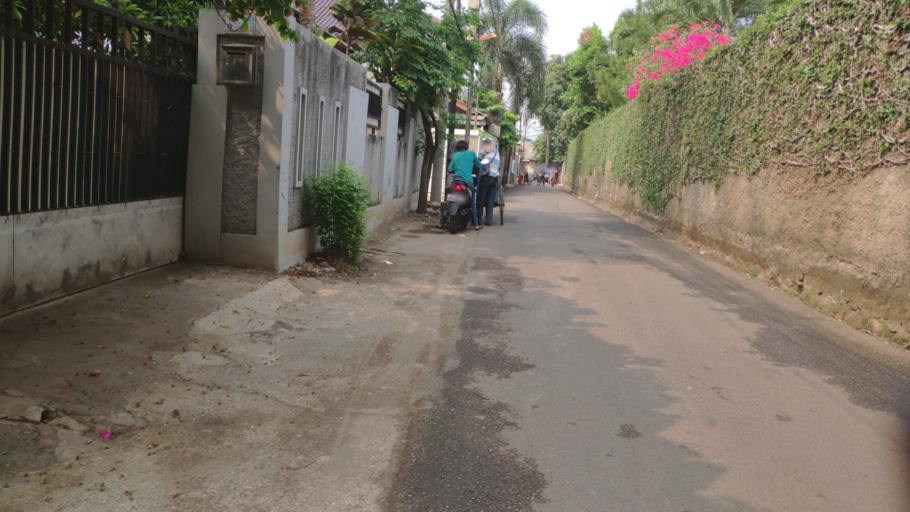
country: ID
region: West Java
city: Depok
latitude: -6.3446
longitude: 106.8080
